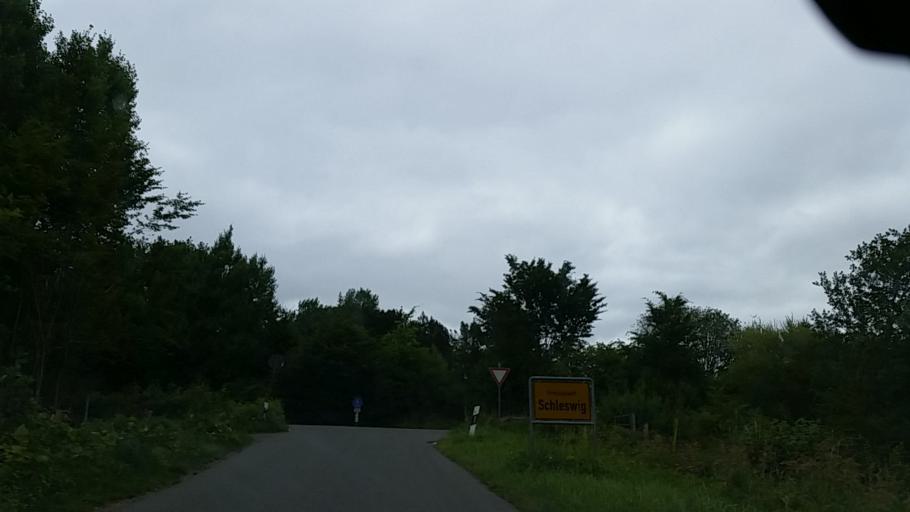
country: DE
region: Schleswig-Holstein
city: Dannewerk
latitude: 54.5033
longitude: 9.5207
